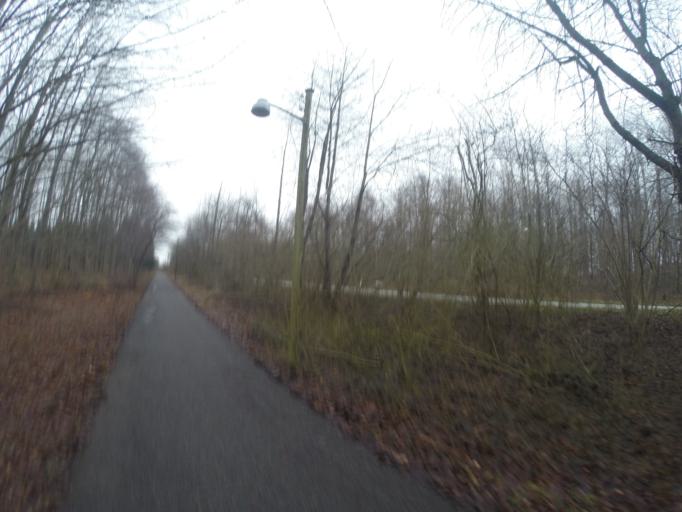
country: DK
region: Capital Region
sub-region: Albertslund Kommune
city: Albertslund
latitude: 55.6851
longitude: 12.3309
